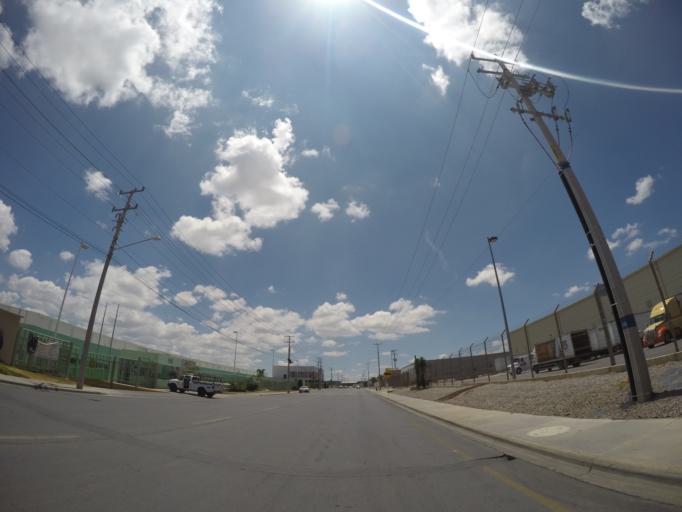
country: MX
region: San Luis Potosi
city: La Pila
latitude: 22.0392
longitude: -100.8916
